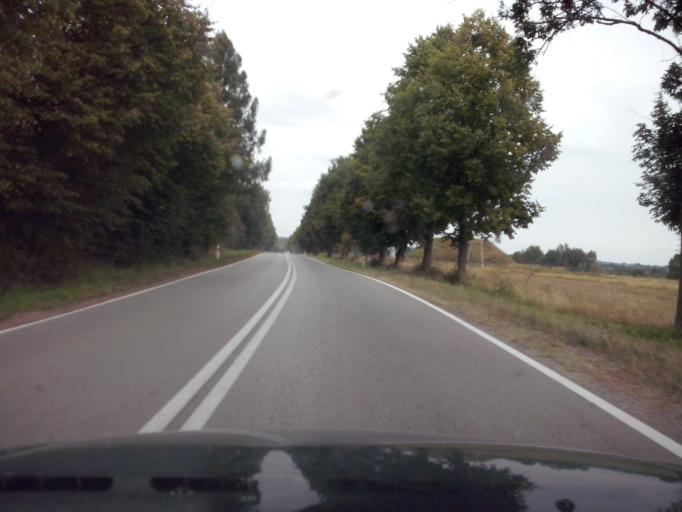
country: PL
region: Swietokrzyskie
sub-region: Powiat kielecki
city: Rakow
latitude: 50.6899
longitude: 21.0592
